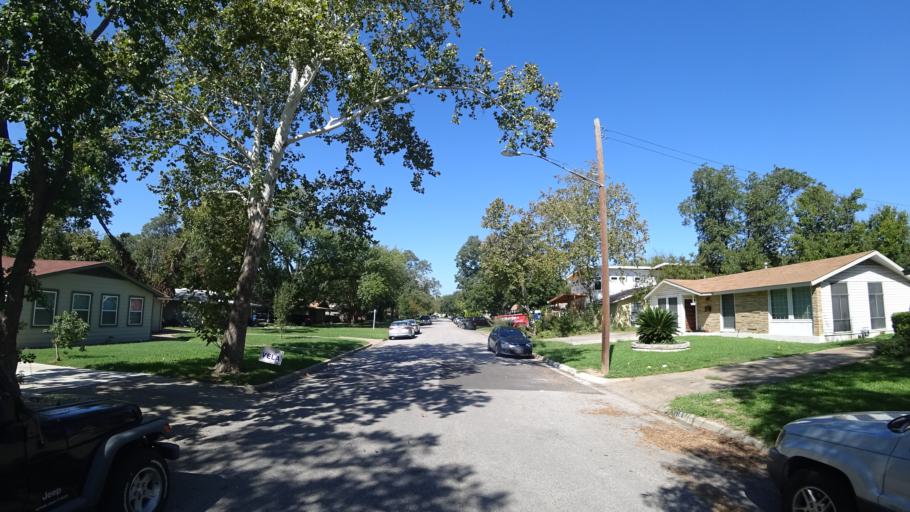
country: US
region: Texas
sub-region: Travis County
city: Austin
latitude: 30.3096
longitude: -97.7005
